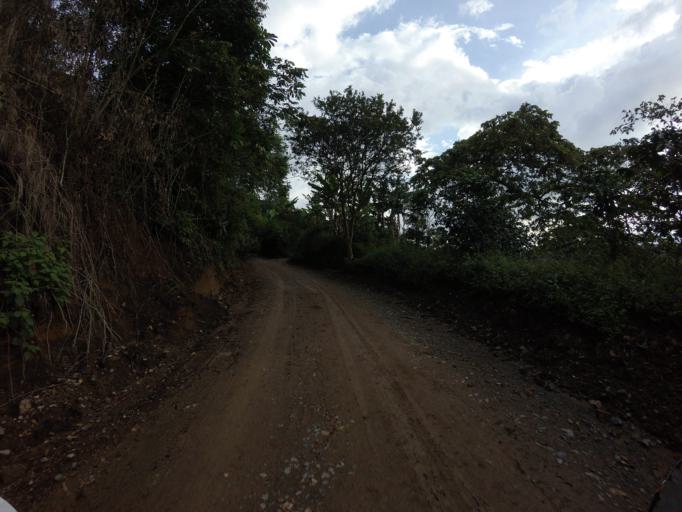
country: CO
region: Valle del Cauca
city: Ulloa
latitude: 4.7082
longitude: -75.7100
